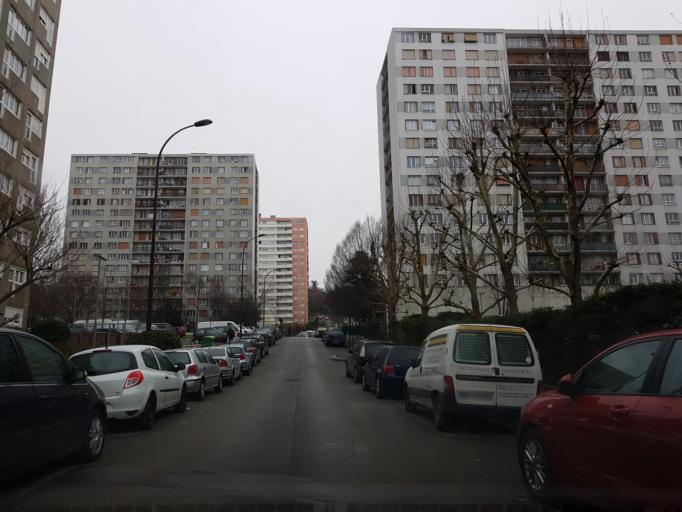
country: FR
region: Ile-de-France
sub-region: Departement du Val-de-Marne
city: Vitry-sur-Seine
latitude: 48.7839
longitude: 2.3918
